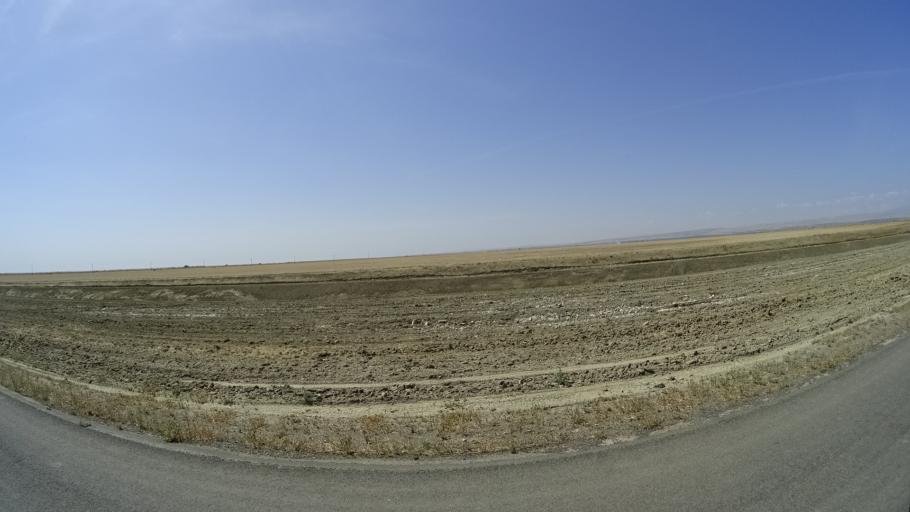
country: US
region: California
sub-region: Kings County
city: Kettleman City
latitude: 36.0940
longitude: -119.9174
